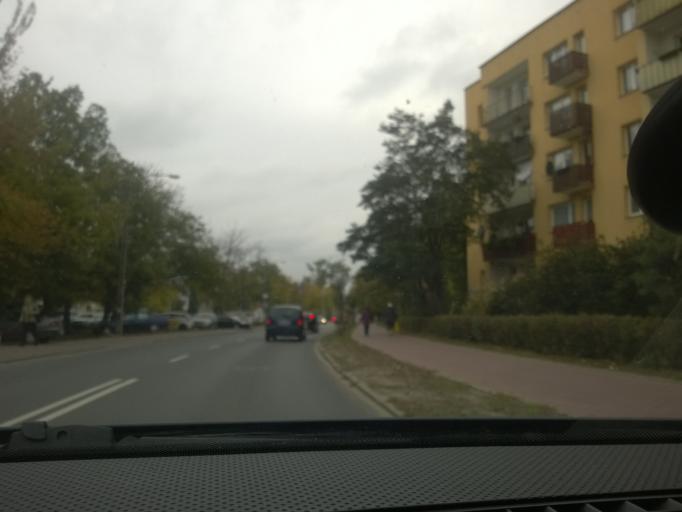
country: PL
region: Masovian Voivodeship
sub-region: Powiat pruszkowski
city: Pruszkow
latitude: 52.1597
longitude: 20.8033
